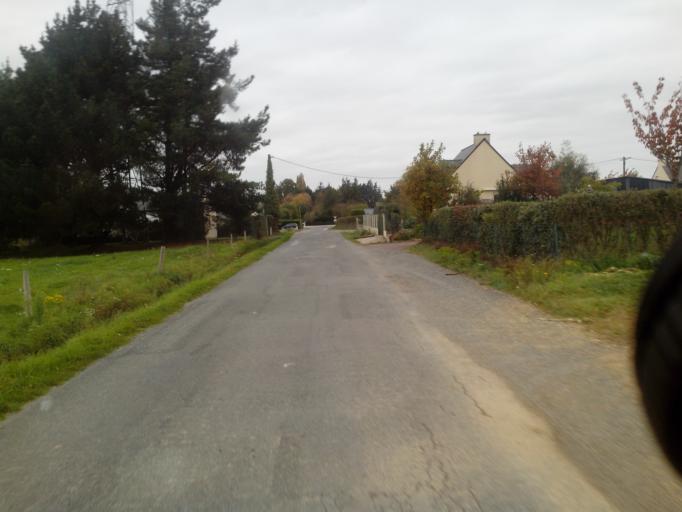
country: FR
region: Brittany
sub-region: Departement du Morbihan
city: Mauron
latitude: 48.0817
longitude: -2.2931
